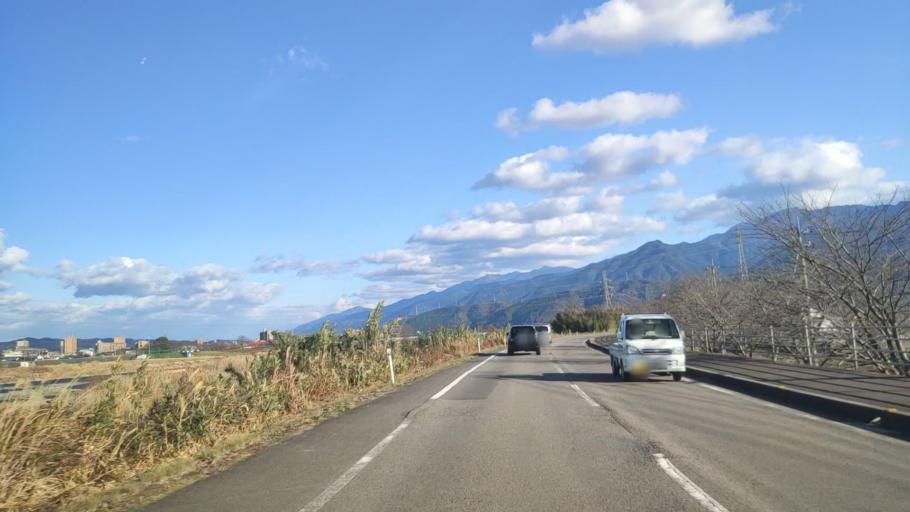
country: JP
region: Ehime
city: Saijo
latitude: 33.9107
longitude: 133.1653
